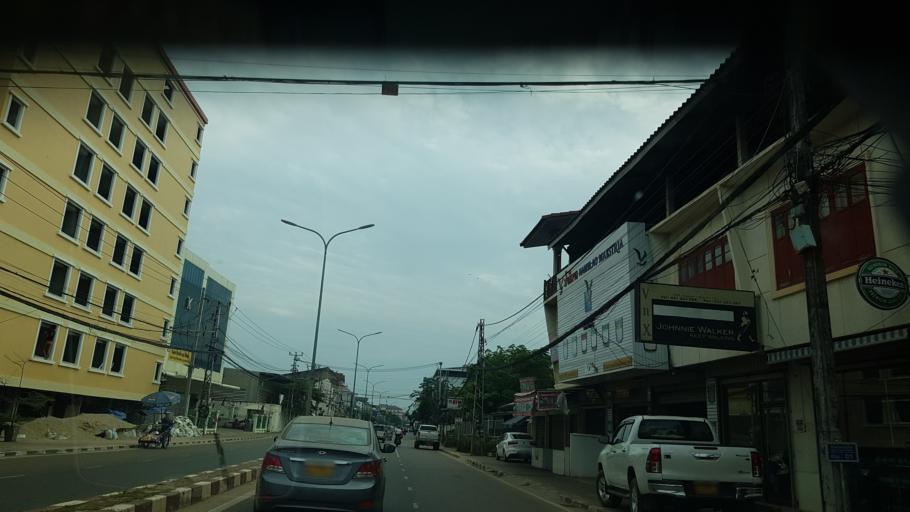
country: LA
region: Vientiane
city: Vientiane
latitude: 17.9564
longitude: 102.6179
